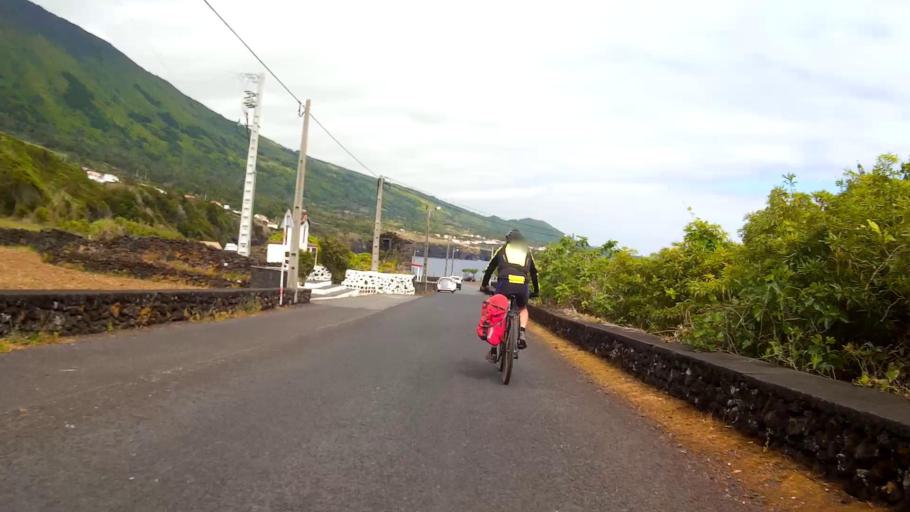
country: PT
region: Azores
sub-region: Sao Roque do Pico
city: Sao Roque do Pico
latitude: 38.4262
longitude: -28.4237
